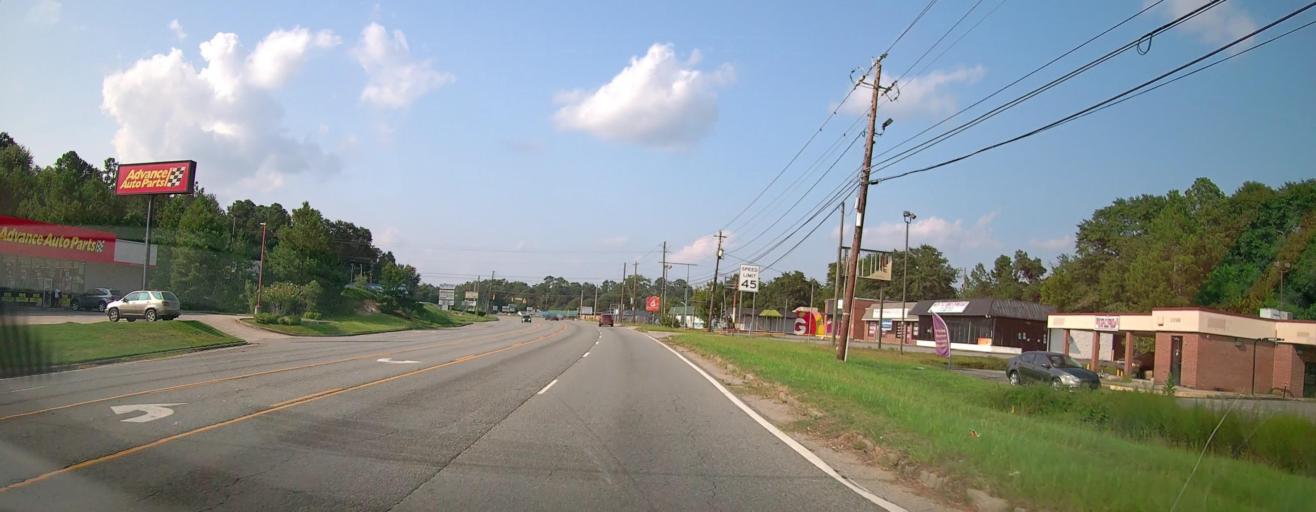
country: US
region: Georgia
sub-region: Bibb County
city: Macon
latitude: 32.8011
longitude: -83.6640
